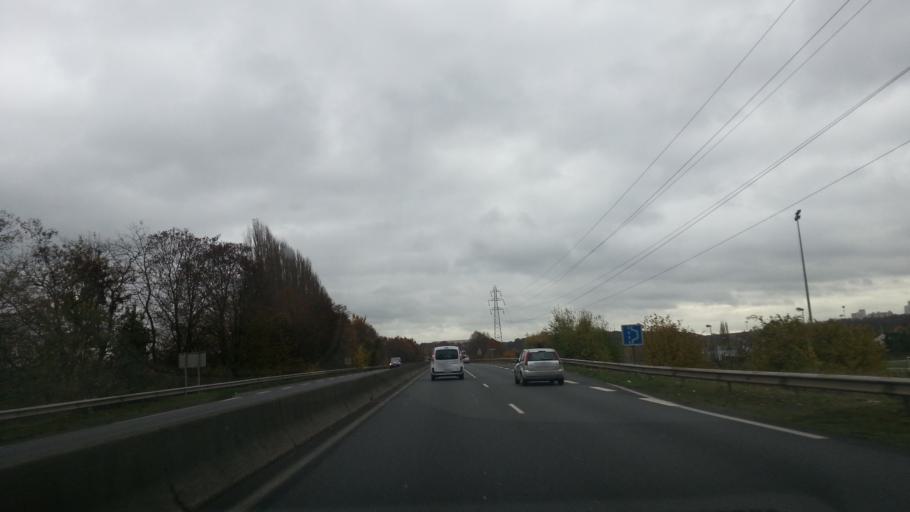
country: FR
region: Picardie
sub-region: Departement de l'Oise
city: Villers-Saint-Paul
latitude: 49.2803
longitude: 2.4806
